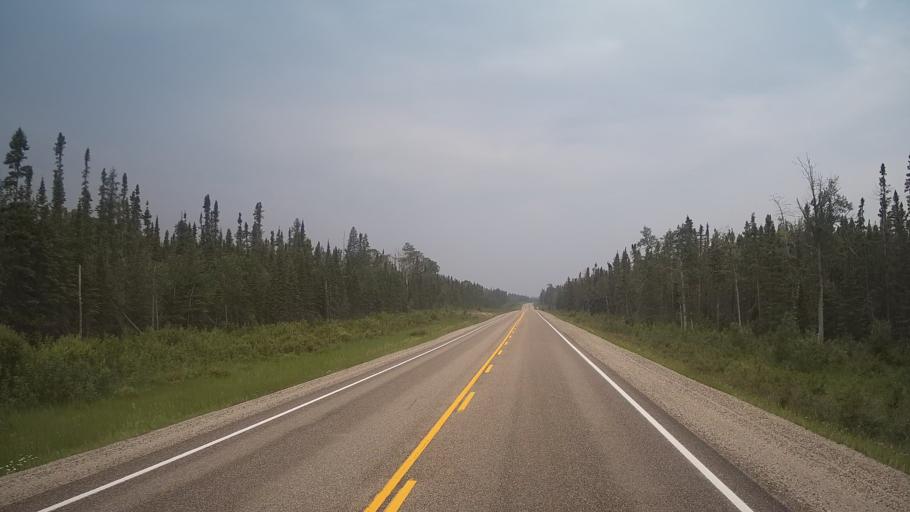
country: CA
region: Ontario
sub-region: Algoma
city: Hornepayne
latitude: 49.7565
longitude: -84.9597
